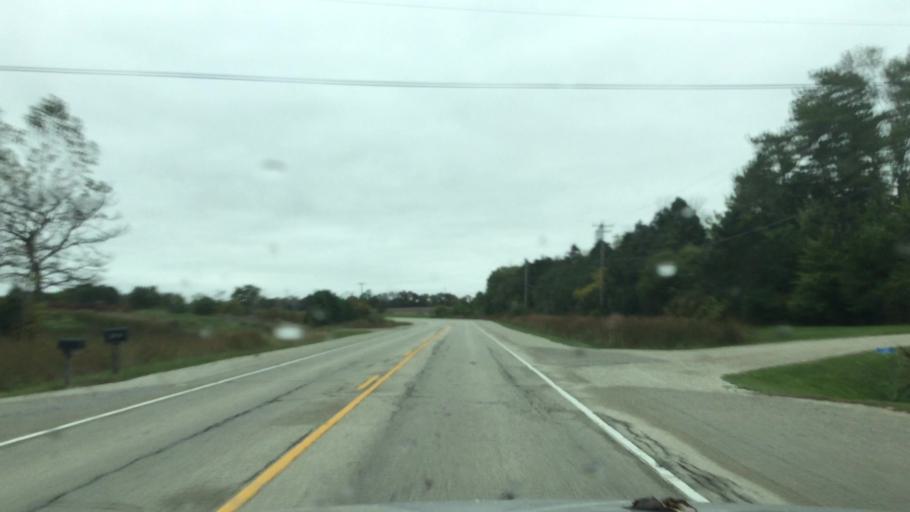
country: US
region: Wisconsin
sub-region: Racine County
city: Eagle Lake
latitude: 42.7403
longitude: -88.1012
